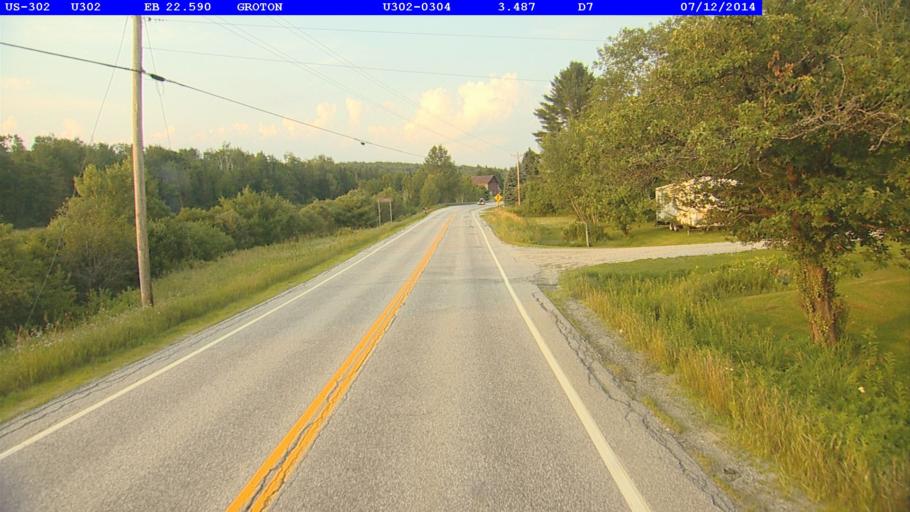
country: US
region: New Hampshire
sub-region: Grafton County
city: Woodsville
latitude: 44.2158
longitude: -72.2496
